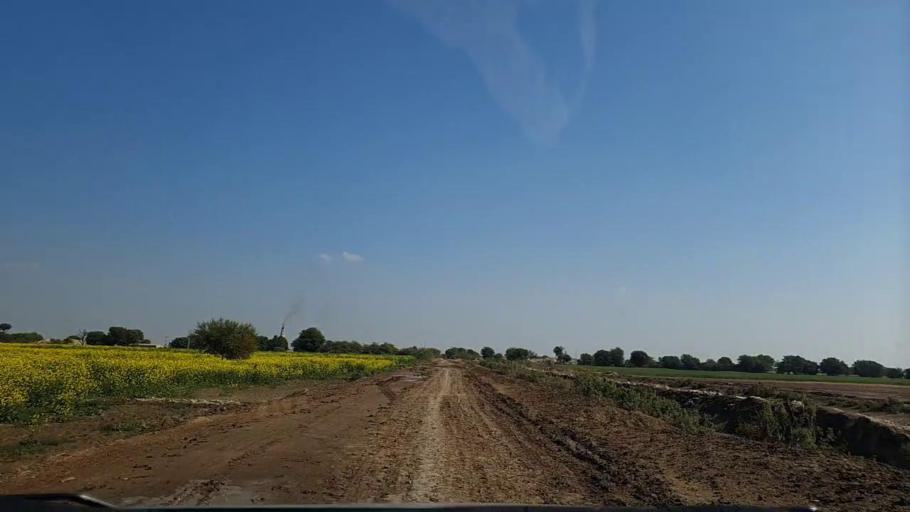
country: PK
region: Sindh
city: Pithoro
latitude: 25.6841
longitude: 69.3583
